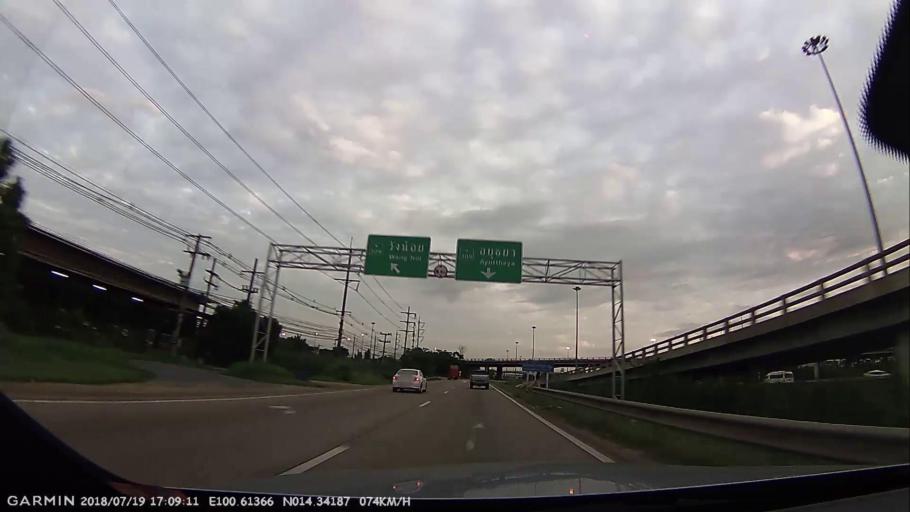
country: TH
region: Phra Nakhon Si Ayutthaya
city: Phra Nakhon Si Ayutthaya
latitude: 14.3418
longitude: 100.6137
